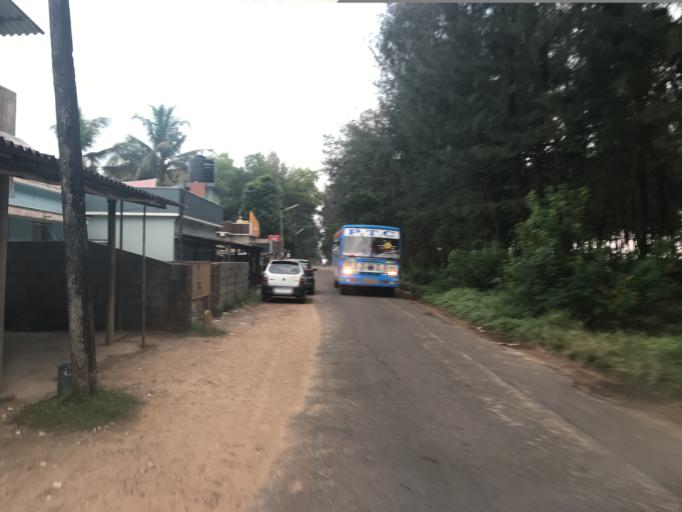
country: IN
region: Karnataka
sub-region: Dakshina Kannada
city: Mangalore
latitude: 12.8882
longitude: 74.8161
